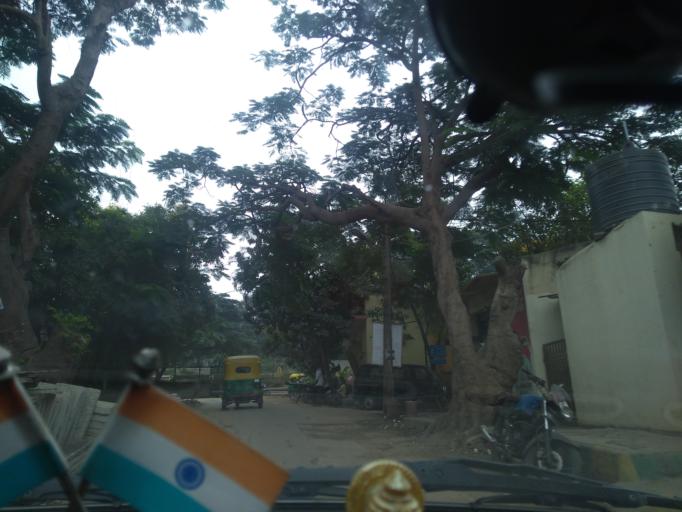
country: IN
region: Karnataka
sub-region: Bangalore Urban
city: Bangalore
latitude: 13.0105
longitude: 77.5588
